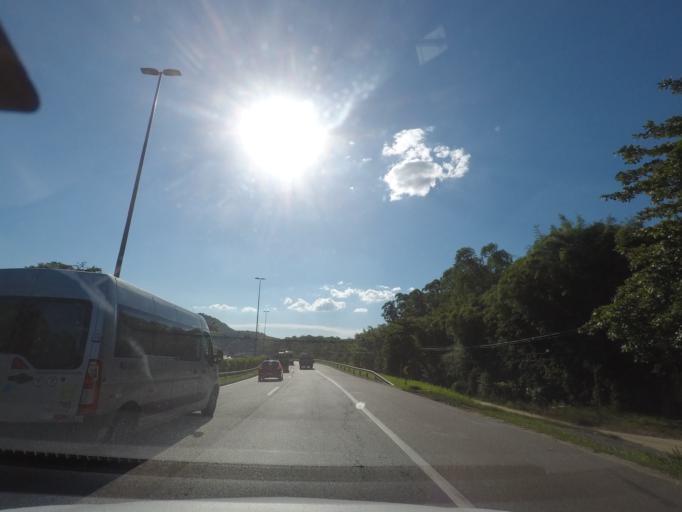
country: BR
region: Rio de Janeiro
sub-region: Petropolis
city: Petropolis
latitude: -22.6558
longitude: -43.1240
